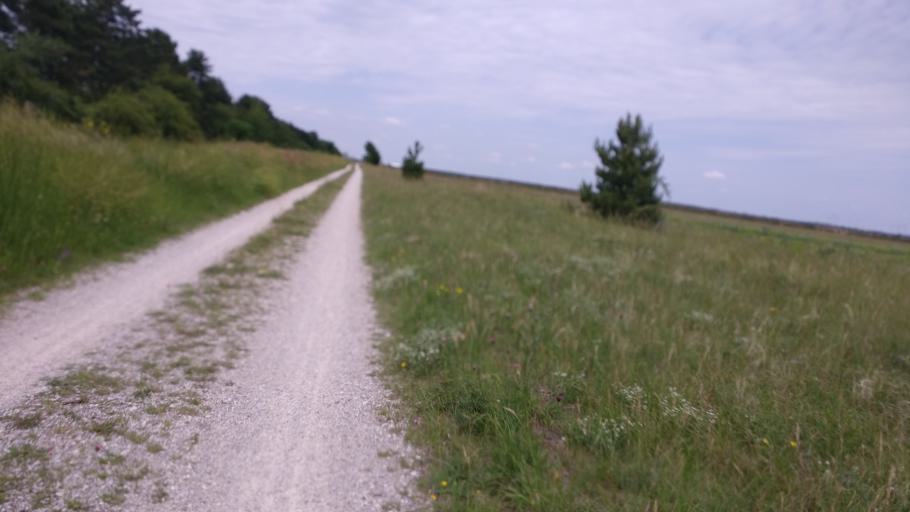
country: AT
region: Lower Austria
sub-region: Politischer Bezirk Wiener Neustadt
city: Lichtenworth
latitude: 47.8683
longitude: 16.2816
